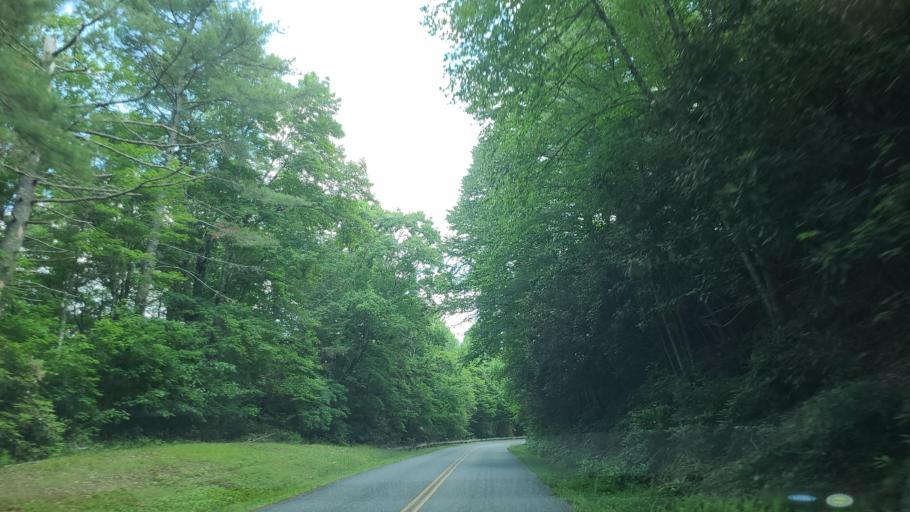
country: US
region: North Carolina
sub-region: Avery County
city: Newland
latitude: 35.9782
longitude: -81.9318
